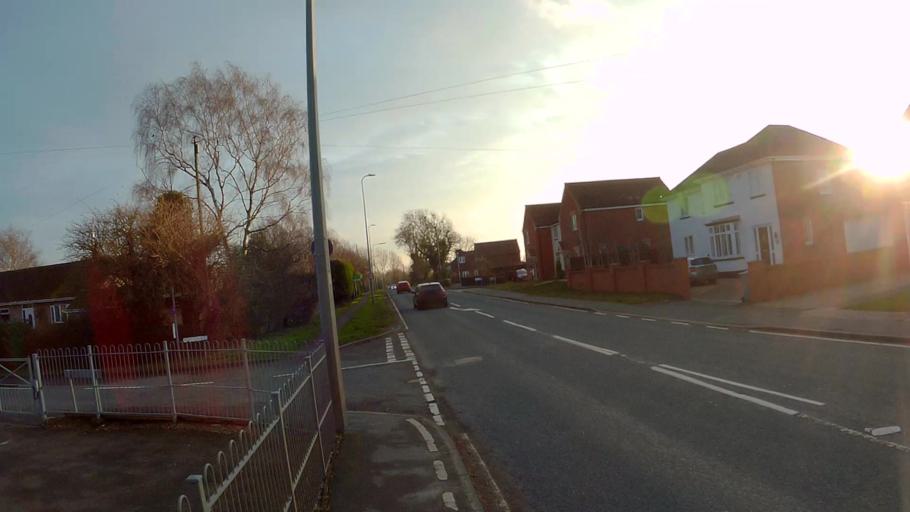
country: GB
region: England
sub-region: Lincolnshire
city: Bourne
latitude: 52.8018
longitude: -0.3798
